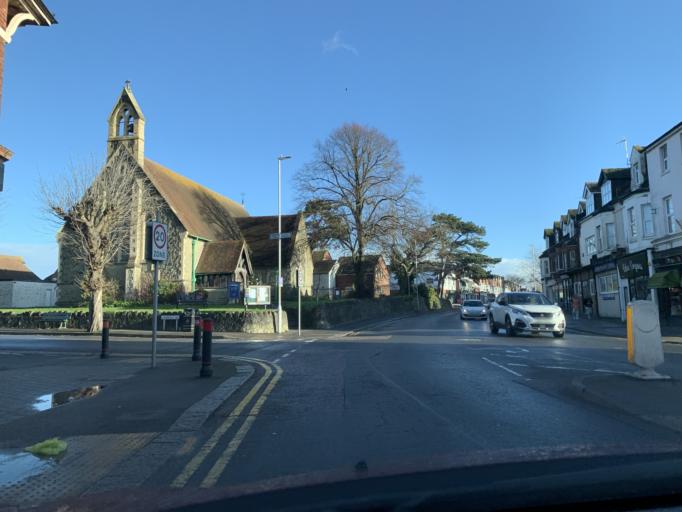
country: GB
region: England
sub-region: Kent
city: Hawkinge
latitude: 51.0881
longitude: 1.1427
